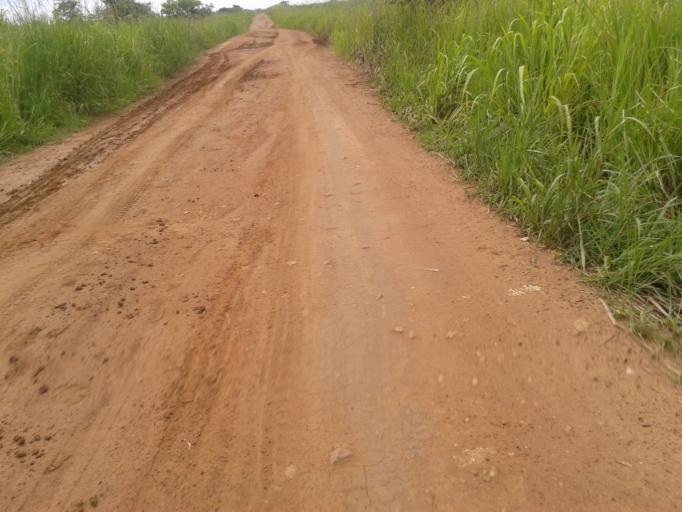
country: UG
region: Northern Region
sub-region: Gulu District
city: Gulu
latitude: 2.8253
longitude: 32.2599
